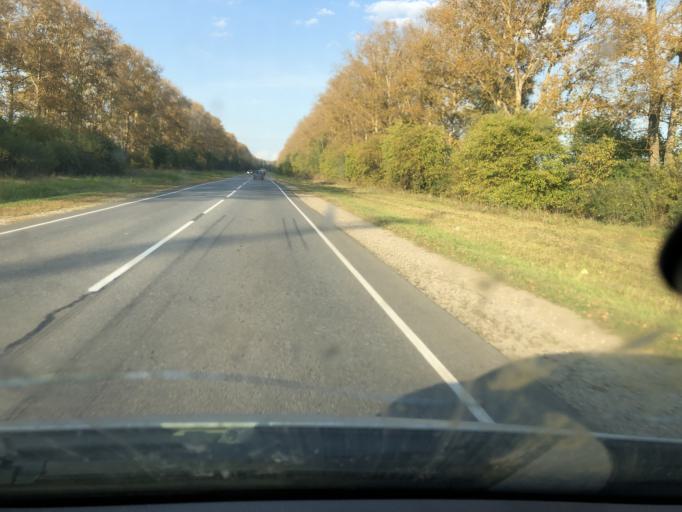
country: RU
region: Kaluga
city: Peremyshl'
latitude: 54.2352
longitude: 36.0653
